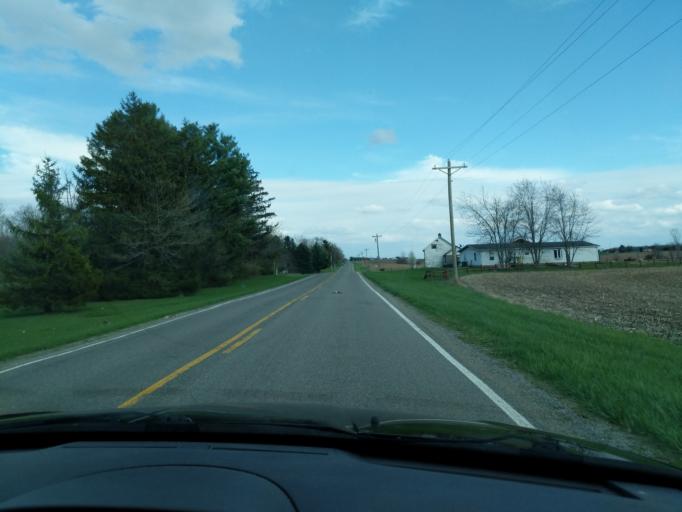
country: US
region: Ohio
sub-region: Champaign County
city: Urbana
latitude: 40.1546
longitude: -83.6541
